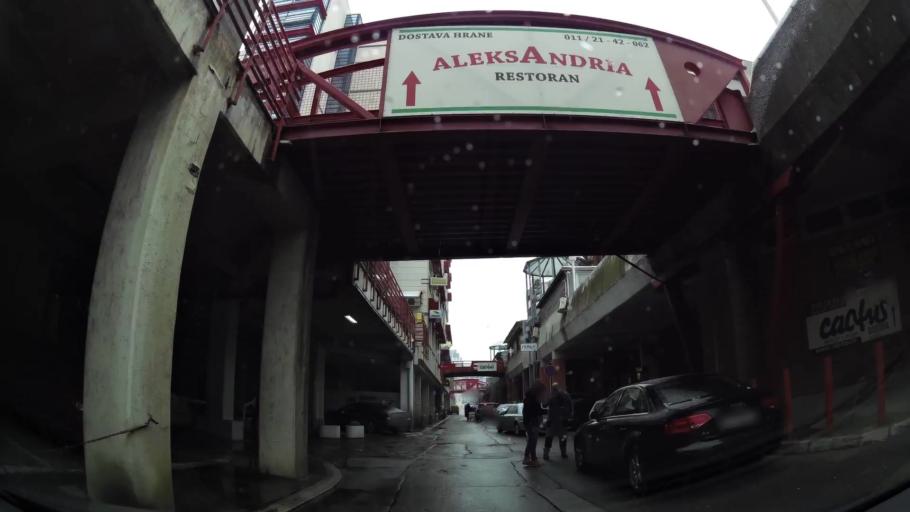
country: RS
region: Central Serbia
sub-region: Belgrade
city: Novi Beograd
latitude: 44.8221
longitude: 20.4201
